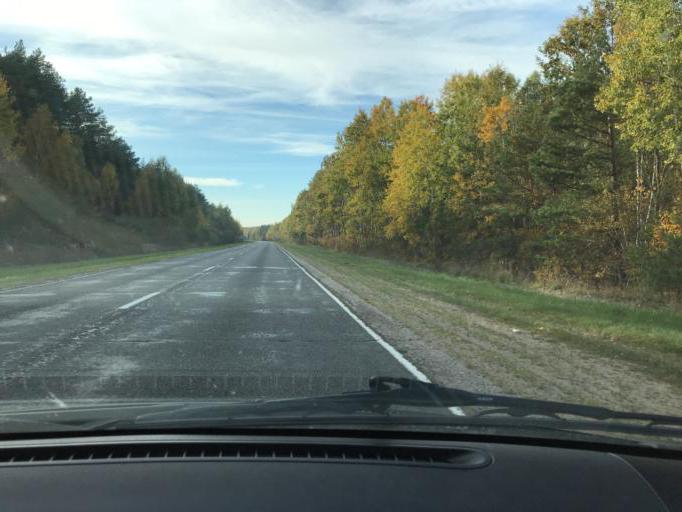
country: BY
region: Brest
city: Ivanava
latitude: 52.1568
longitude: 25.7678
